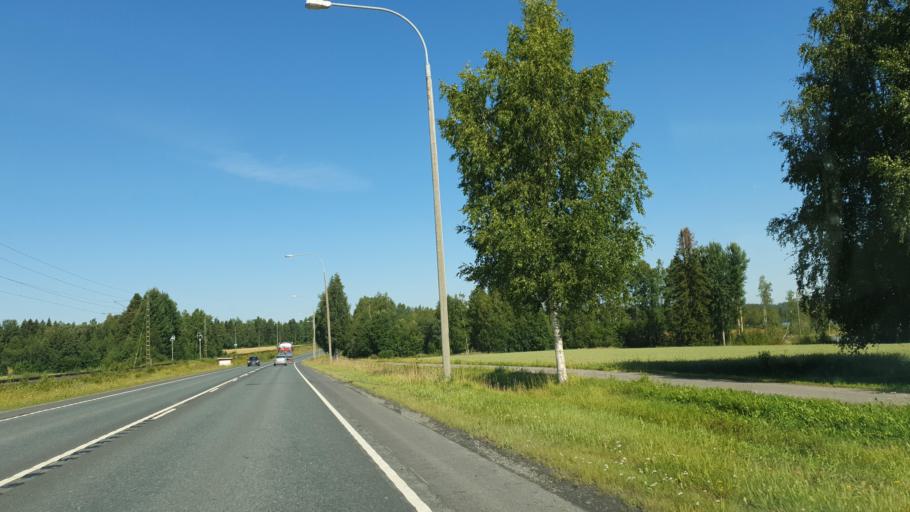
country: FI
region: Northern Savo
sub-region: Ylae-Savo
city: Lapinlahti
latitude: 63.2554
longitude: 27.4748
